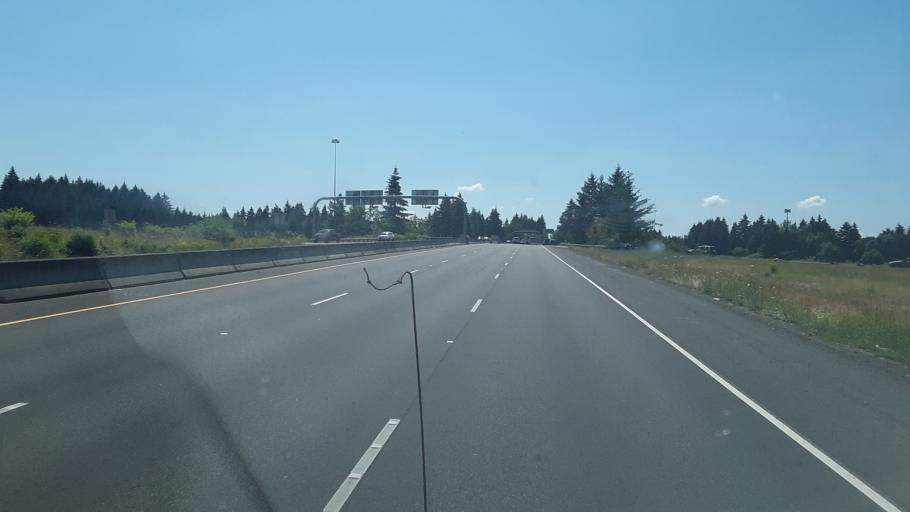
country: US
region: Washington
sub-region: Clark County
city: Orchards
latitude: 45.6582
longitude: -122.5678
